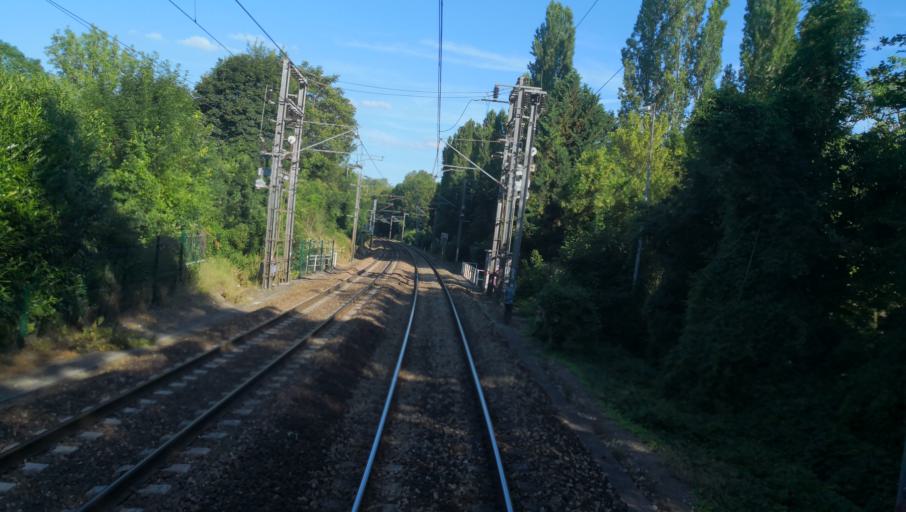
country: FR
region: Ile-de-France
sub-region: Departement des Yvelines
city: Villennes-sur-Seine
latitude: 48.9313
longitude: 2.0064
